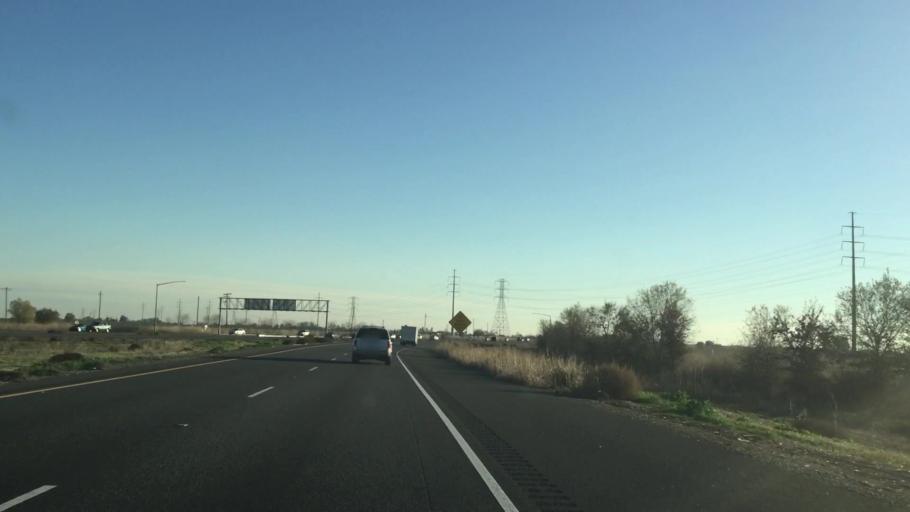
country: US
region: California
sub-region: Sacramento County
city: Elverta
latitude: 38.8468
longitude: -121.5447
